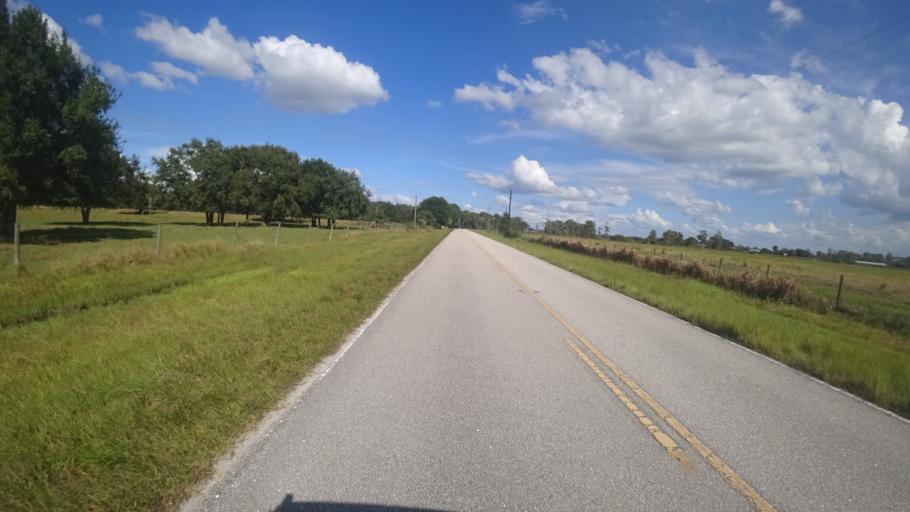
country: US
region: Florida
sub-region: DeSoto County
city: Nocatee
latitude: 27.2708
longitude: -82.0817
